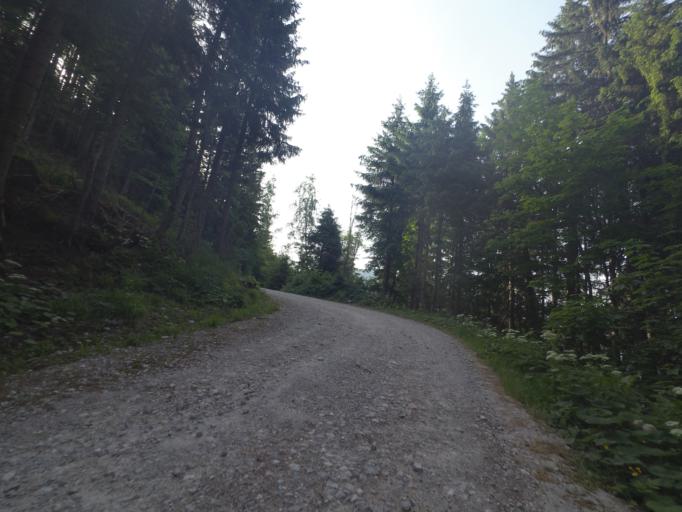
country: AT
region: Salzburg
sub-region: Politischer Bezirk Sankt Johann im Pongau
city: Muhlbach am Hochkonig
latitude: 47.3602
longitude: 13.1122
